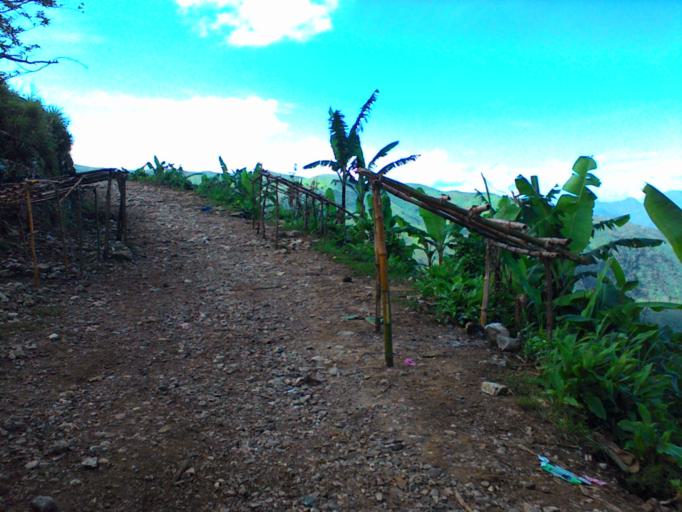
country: HT
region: Grandans
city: Moron
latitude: 18.4676
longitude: -74.1167
